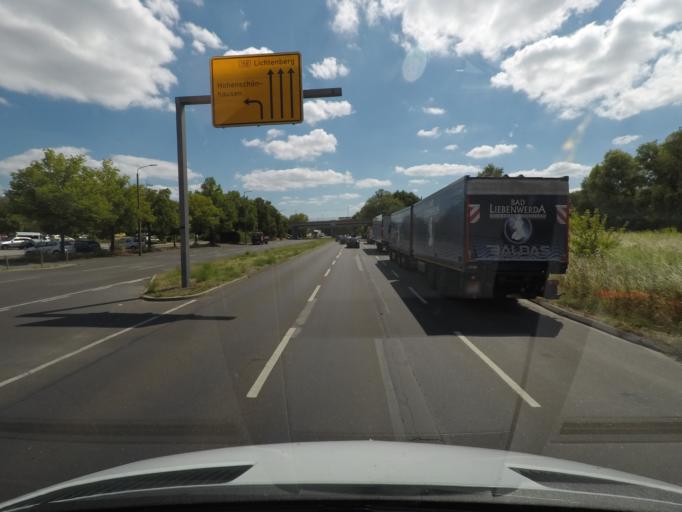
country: DE
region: Berlin
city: Biesdorf
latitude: 52.5270
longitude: 13.5374
